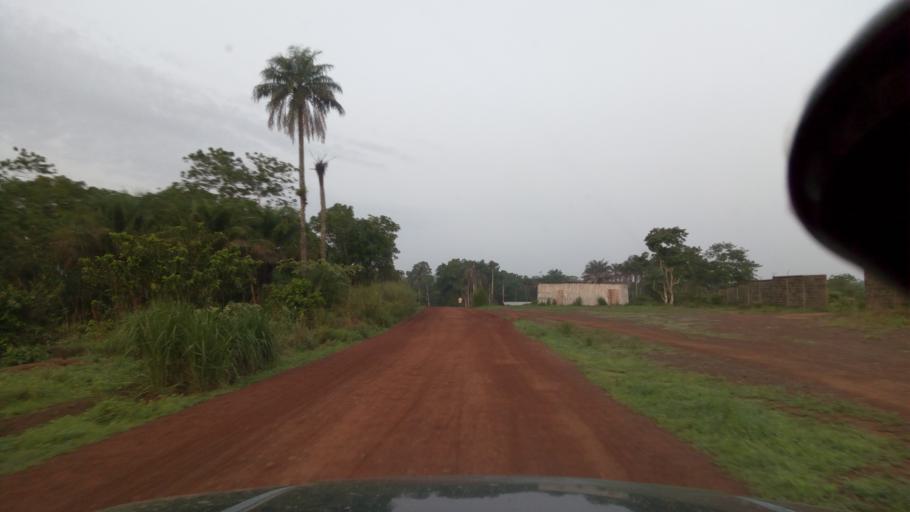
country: SL
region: Northern Province
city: Port Loko
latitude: 8.7488
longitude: -12.7895
